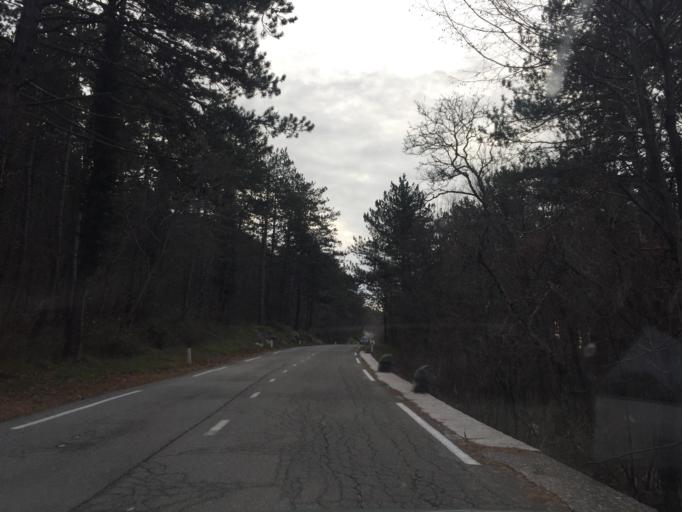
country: SI
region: Nova Gorica
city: Sempas
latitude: 45.9756
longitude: 13.7184
